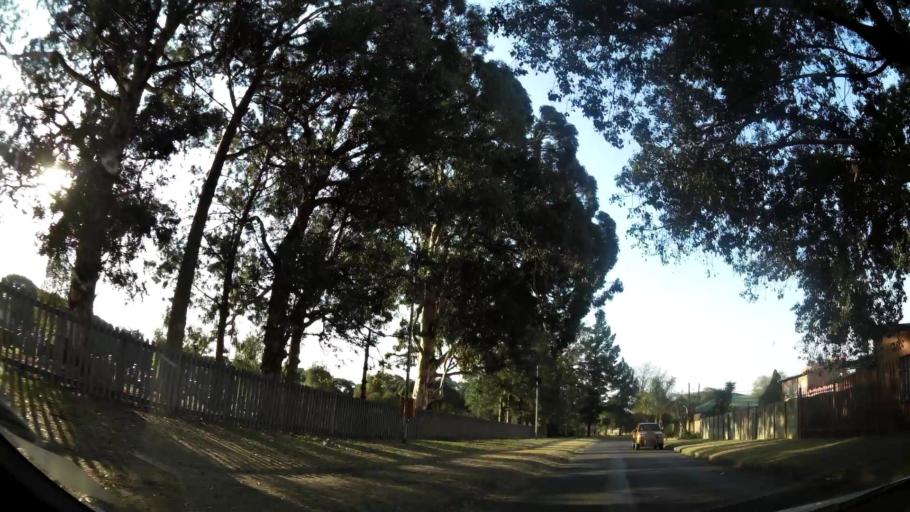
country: ZA
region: Gauteng
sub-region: Ekurhuleni Metropolitan Municipality
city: Springs
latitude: -26.2538
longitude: 28.3837
